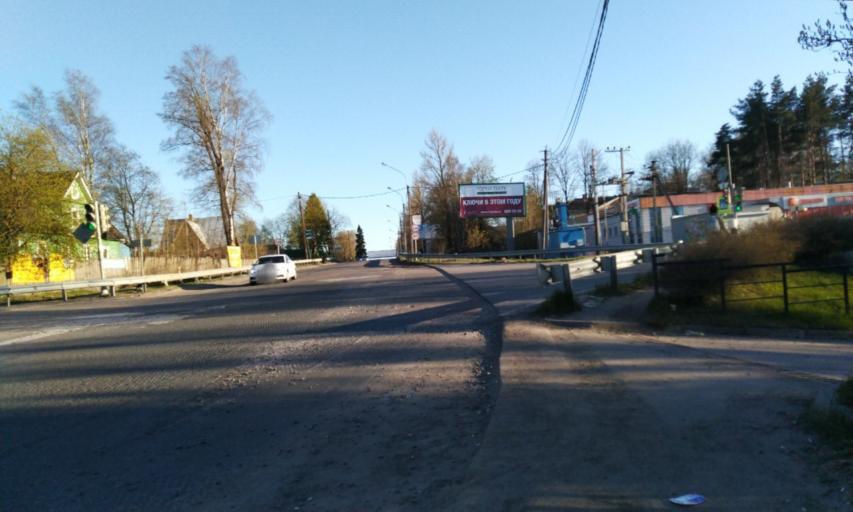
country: RU
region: Leningrad
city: Toksovo
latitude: 60.1120
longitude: 30.5016
